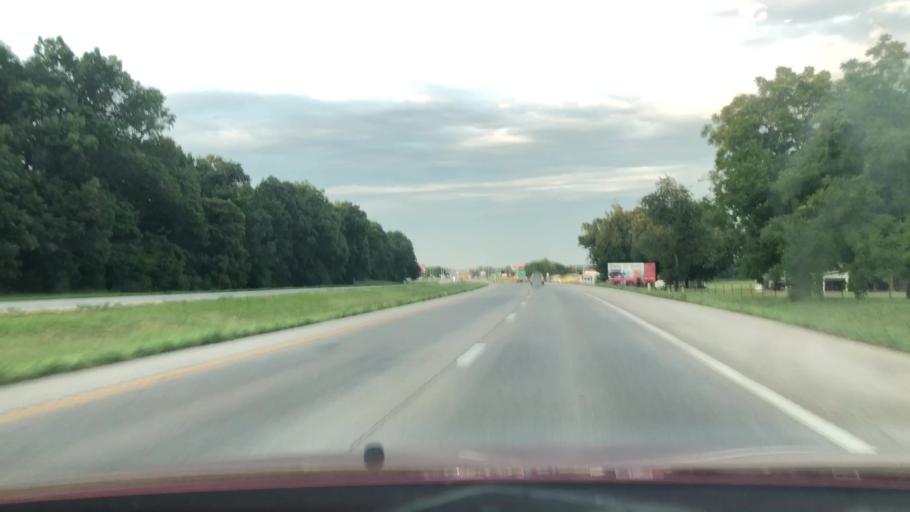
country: US
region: Missouri
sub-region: Greene County
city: Republic
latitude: 37.1421
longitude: -93.4362
